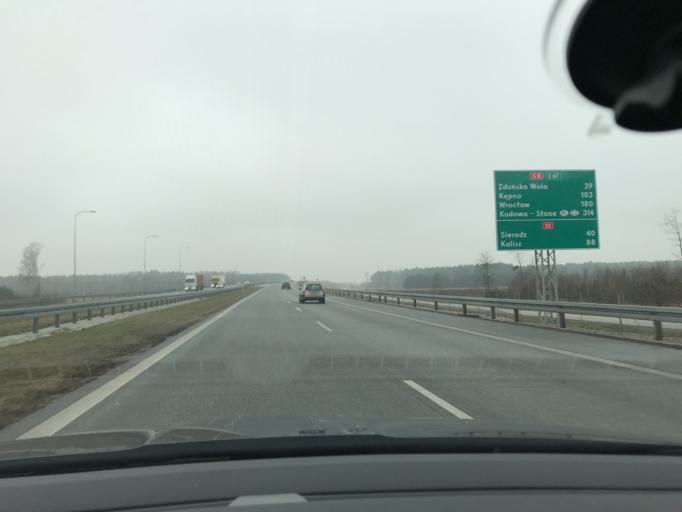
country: PL
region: Lodz Voivodeship
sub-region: Powiat laski
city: Lask
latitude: 51.5719
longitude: 19.1730
